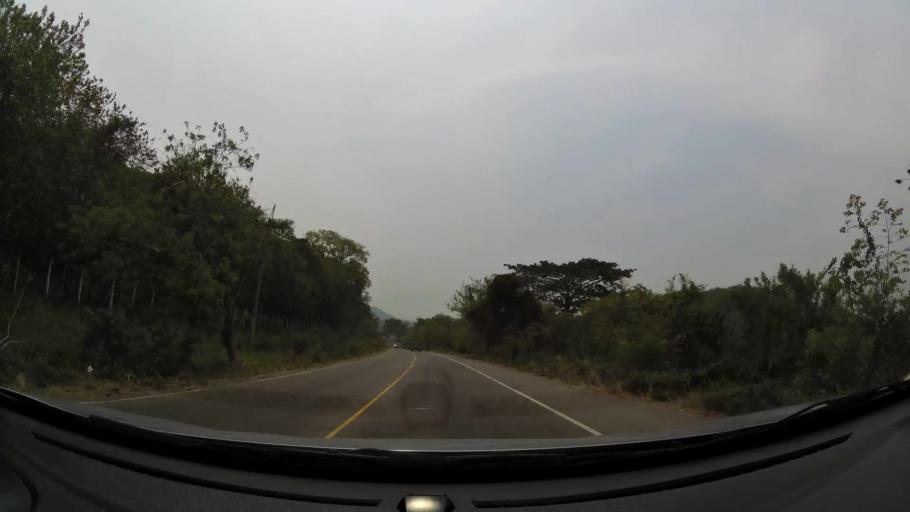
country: HN
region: Cortes
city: Bejuco
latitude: 15.1690
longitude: -87.9516
